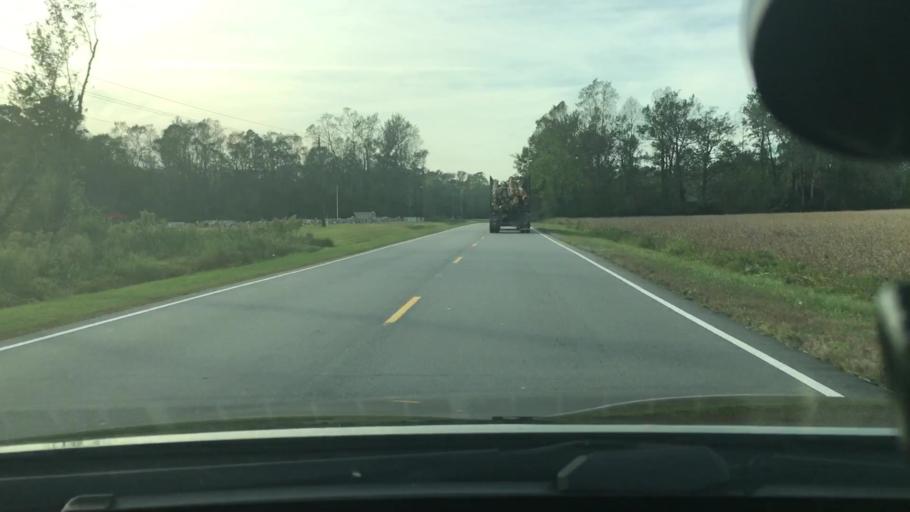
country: US
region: North Carolina
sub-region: Craven County
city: Vanceboro
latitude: 35.2933
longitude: -77.1393
